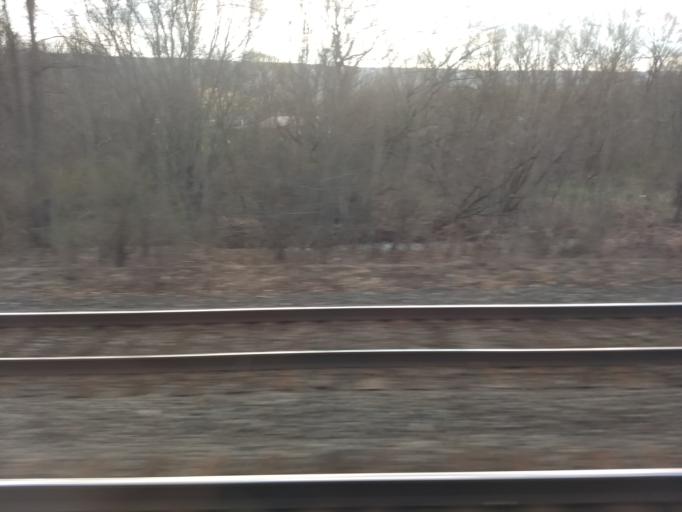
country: US
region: Pennsylvania
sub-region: Blair County
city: Bellwood
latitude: 40.5901
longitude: -78.3427
